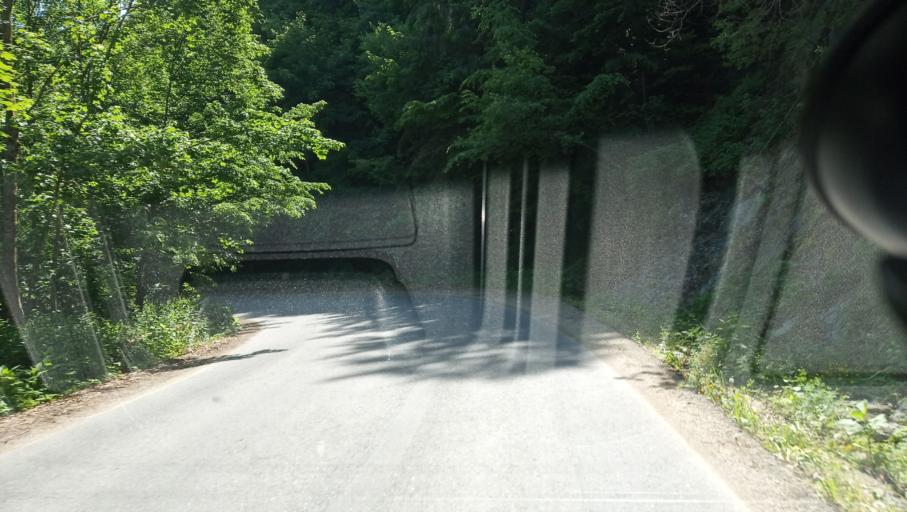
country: RO
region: Cluj
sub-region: Comuna Capusu Mare
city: Capusu Mare
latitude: 46.7260
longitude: 23.2876
